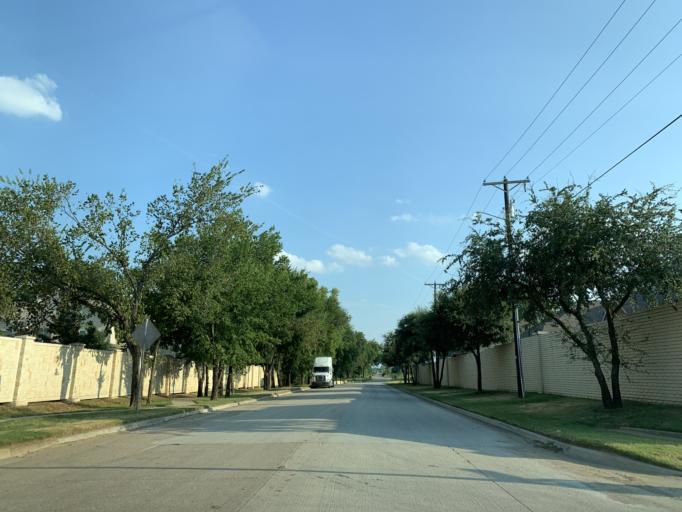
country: US
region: Texas
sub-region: Tarrant County
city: Hurst
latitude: 32.8009
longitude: -97.1691
